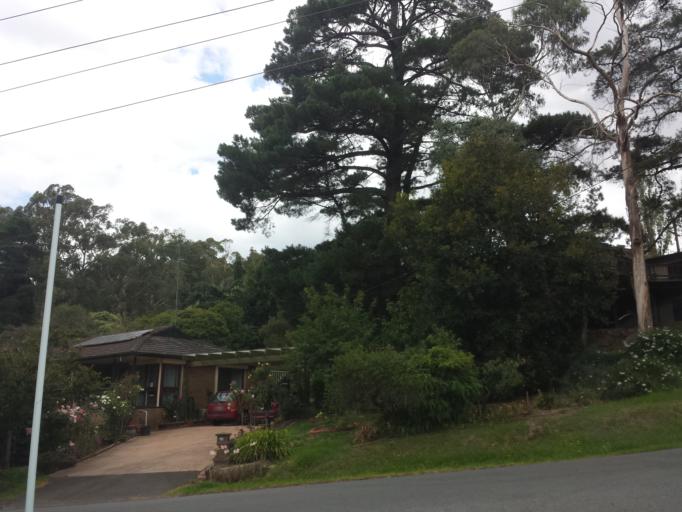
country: AU
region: Victoria
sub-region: Yarra Ranges
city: Belgrave Heights
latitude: -37.9171
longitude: 145.3587
